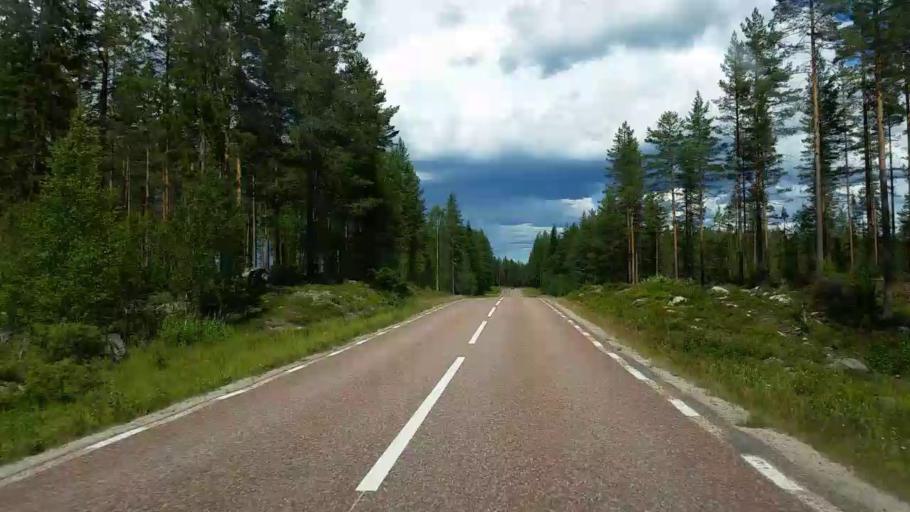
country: SE
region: Gaevleborg
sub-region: Ovanakers Kommun
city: Edsbyn
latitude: 61.3166
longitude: 15.5096
